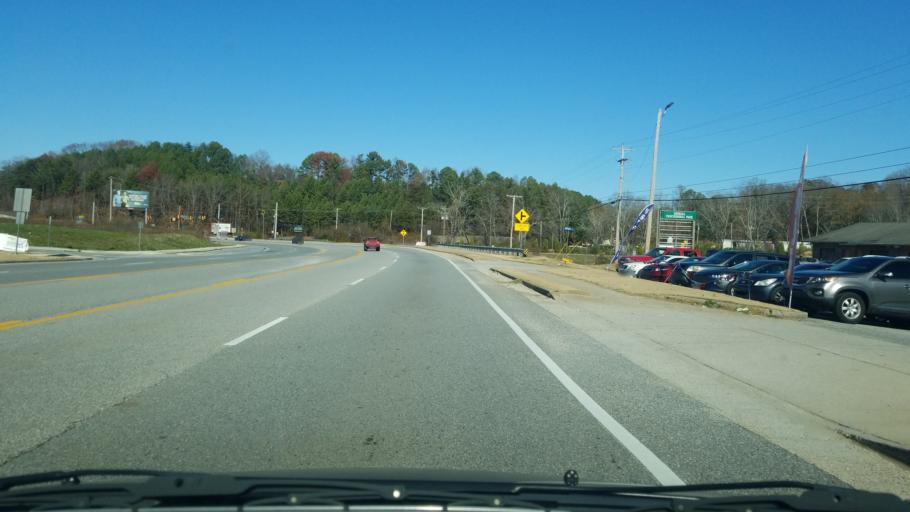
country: US
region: Georgia
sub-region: Catoosa County
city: Indian Springs
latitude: 34.9836
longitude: -85.1872
